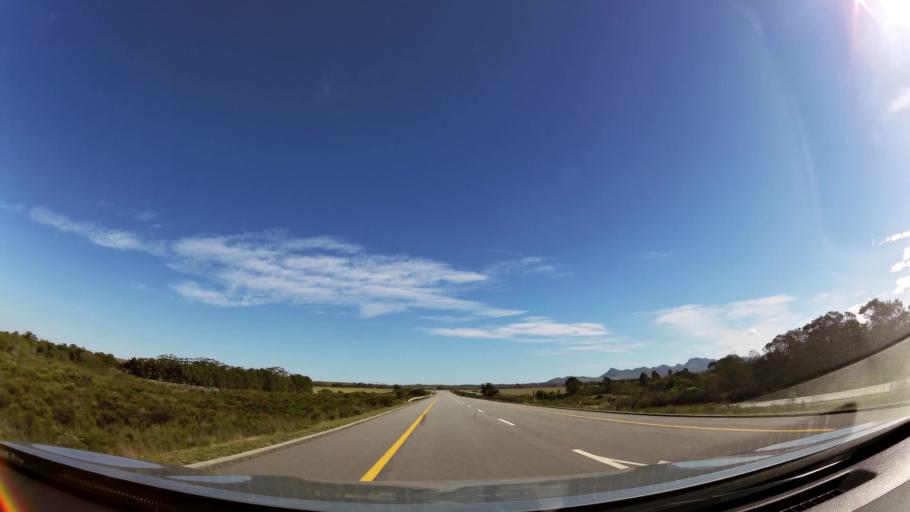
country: ZA
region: Eastern Cape
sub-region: Cacadu District Municipality
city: Kruisfontein
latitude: -34.0282
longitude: 24.6020
